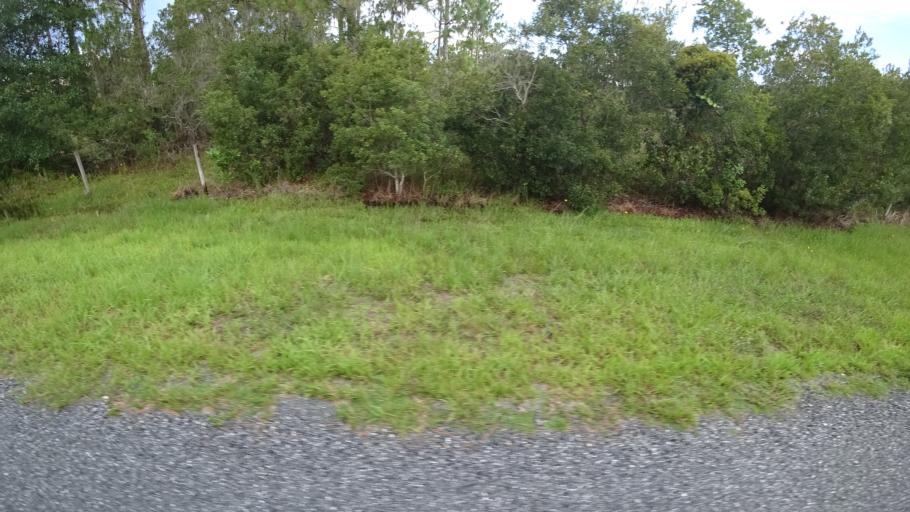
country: US
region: Florida
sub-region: Sarasota County
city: Lake Sarasota
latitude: 27.3970
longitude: -82.2793
